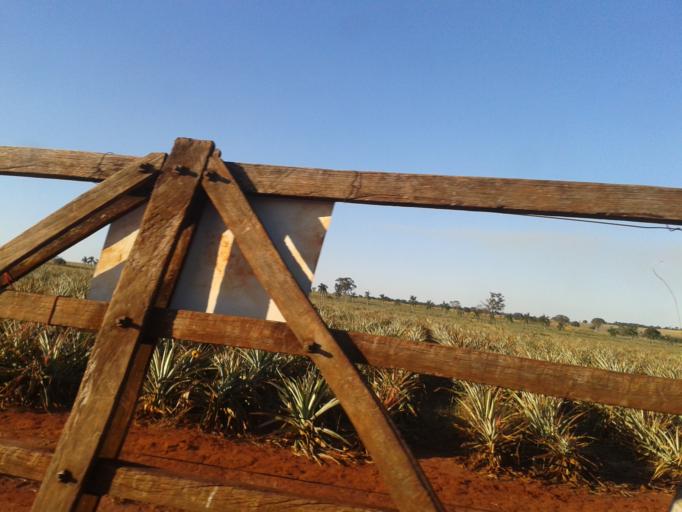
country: BR
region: Minas Gerais
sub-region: Centralina
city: Centralina
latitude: -18.7597
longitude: -49.2019
